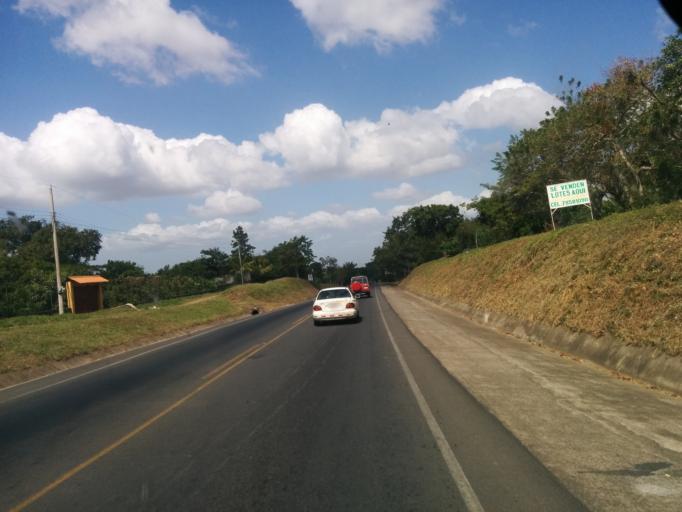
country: NI
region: Masaya
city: Masaya
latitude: 11.9483
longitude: -86.0917
